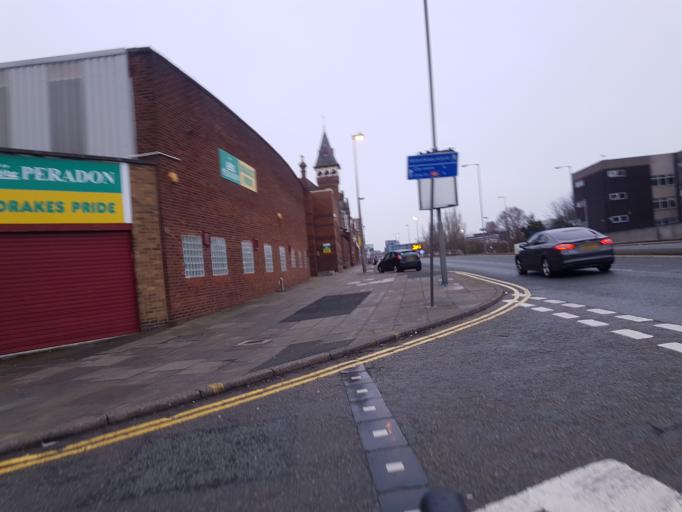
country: GB
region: England
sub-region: Liverpool
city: Liverpool
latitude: 53.4146
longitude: -2.9782
